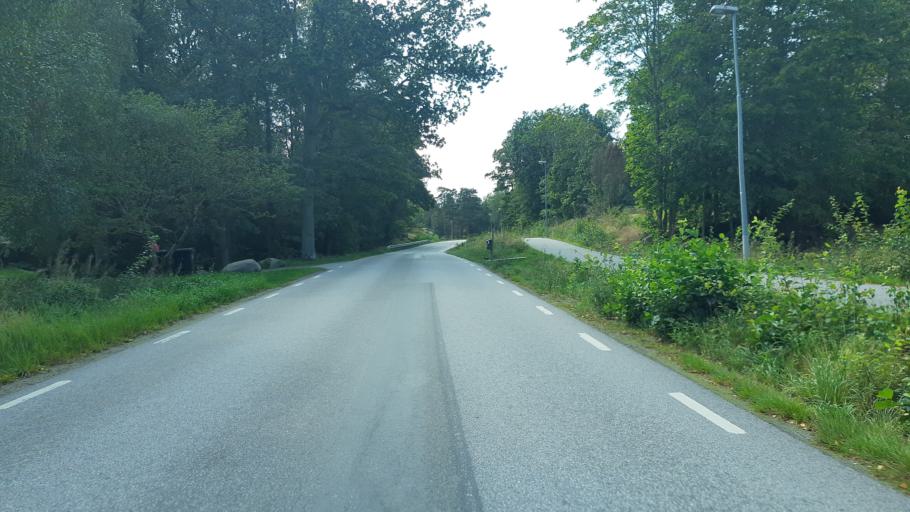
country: SE
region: Blekinge
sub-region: Ronneby Kommun
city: Ronneby
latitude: 56.1768
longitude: 15.2486
